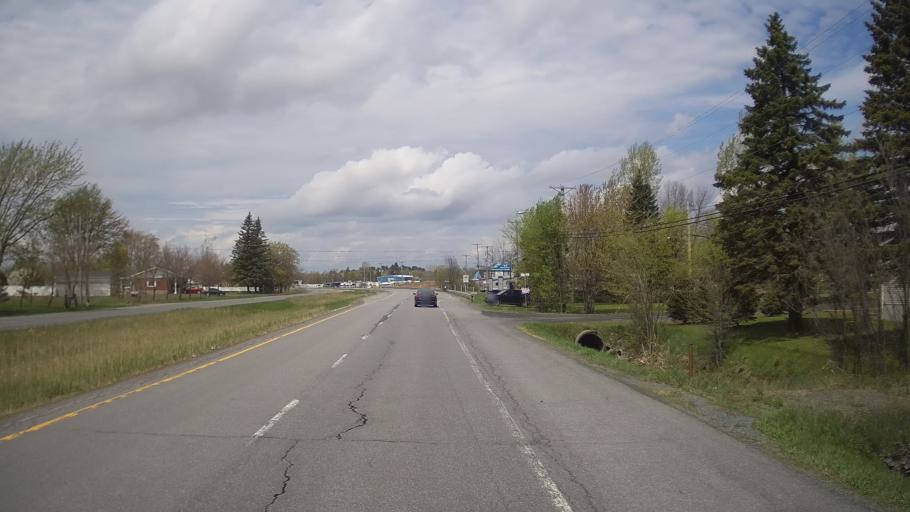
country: CA
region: Quebec
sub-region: Monteregie
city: Carignan
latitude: 45.3738
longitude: -73.3518
